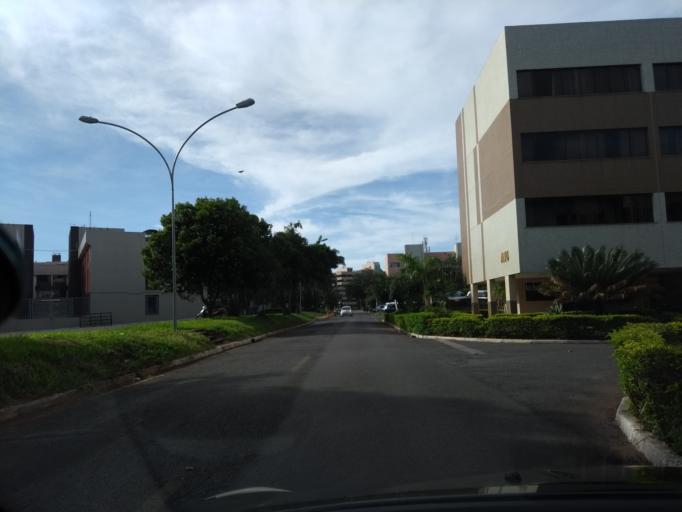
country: BR
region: Federal District
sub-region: Brasilia
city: Brasilia
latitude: -15.7932
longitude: -47.9292
